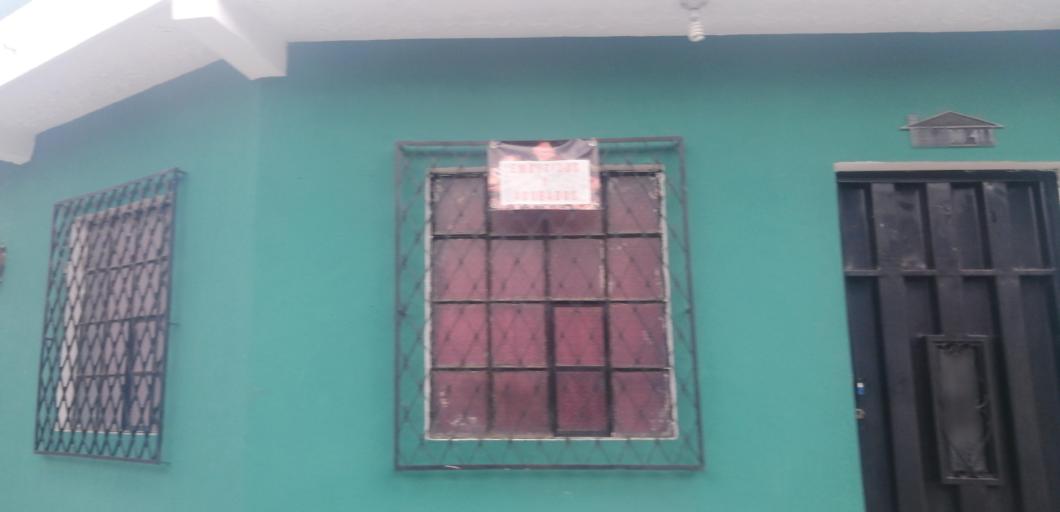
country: GT
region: Quetzaltenango
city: Quetzaltenango
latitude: 14.8296
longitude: -91.5302
